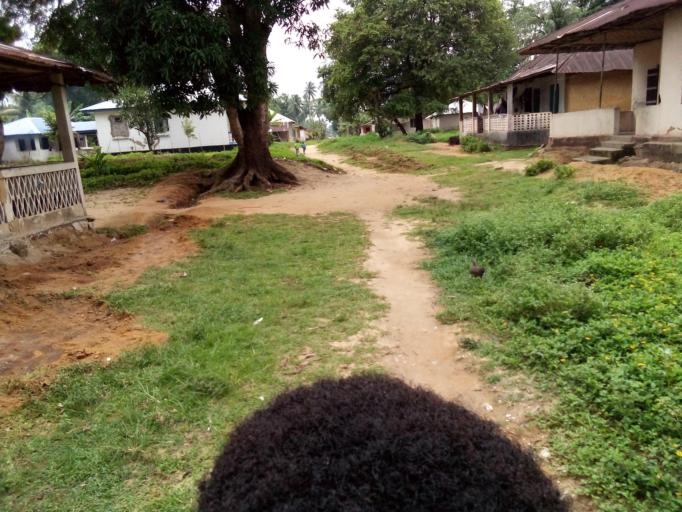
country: SL
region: Southern Province
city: Bonthe
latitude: 7.5219
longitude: -12.5045
